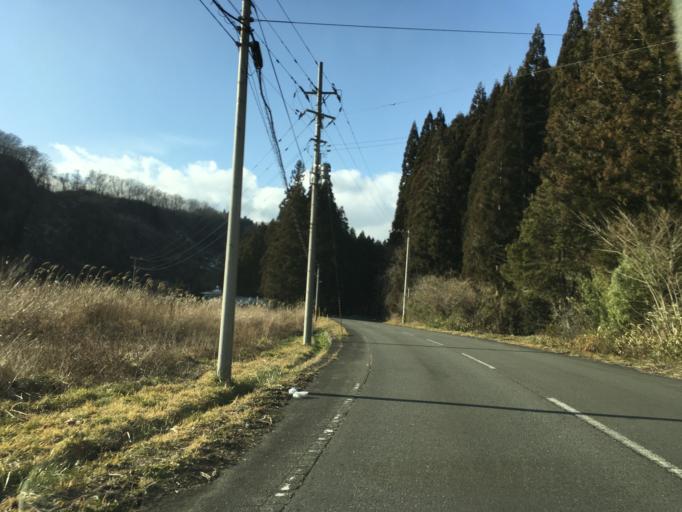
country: JP
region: Miyagi
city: Furukawa
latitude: 38.8020
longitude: 140.8335
